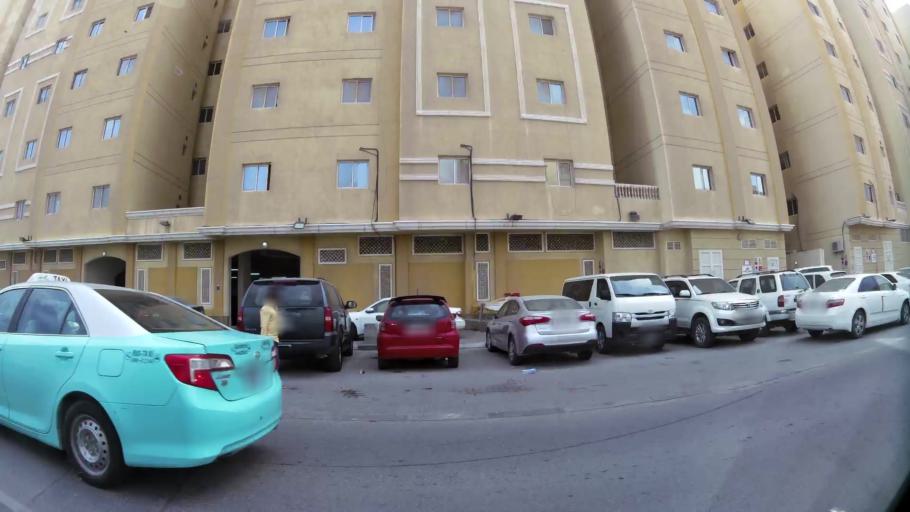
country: QA
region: Baladiyat ad Dawhah
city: Doha
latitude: 25.2847
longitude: 51.5012
